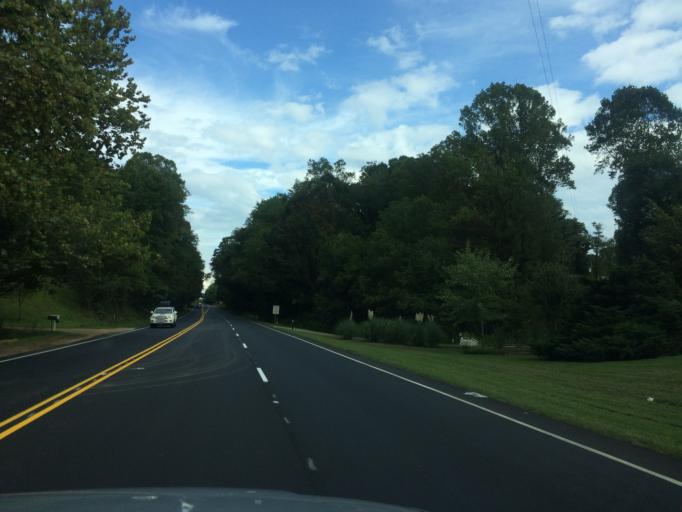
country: US
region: North Carolina
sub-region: Haywood County
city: Canton
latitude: 35.5390
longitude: -82.7655
